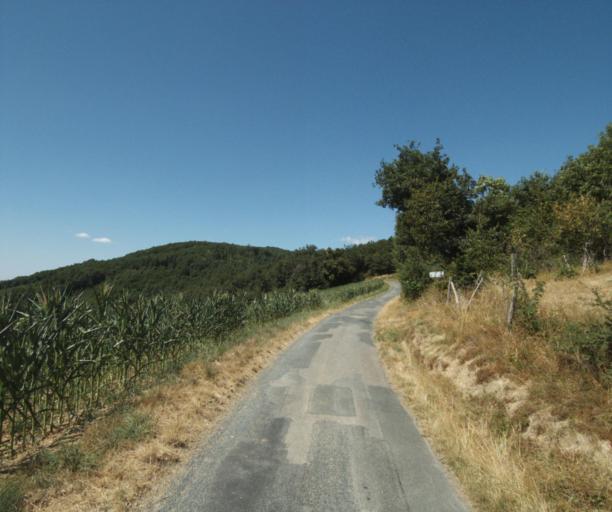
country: FR
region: Rhone-Alpes
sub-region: Departement du Rhone
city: Bessenay
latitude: 45.7776
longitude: 4.5172
